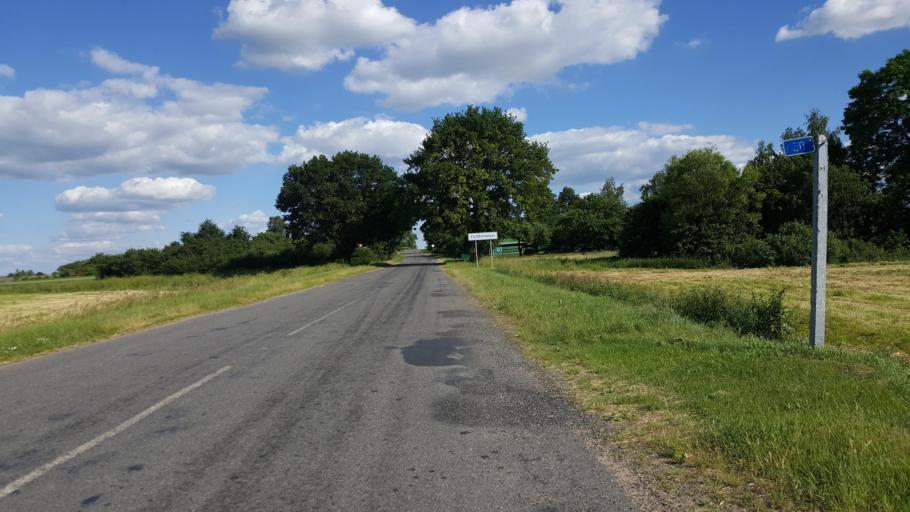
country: BY
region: Brest
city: Kamyanyets
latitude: 52.4677
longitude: 23.7129
